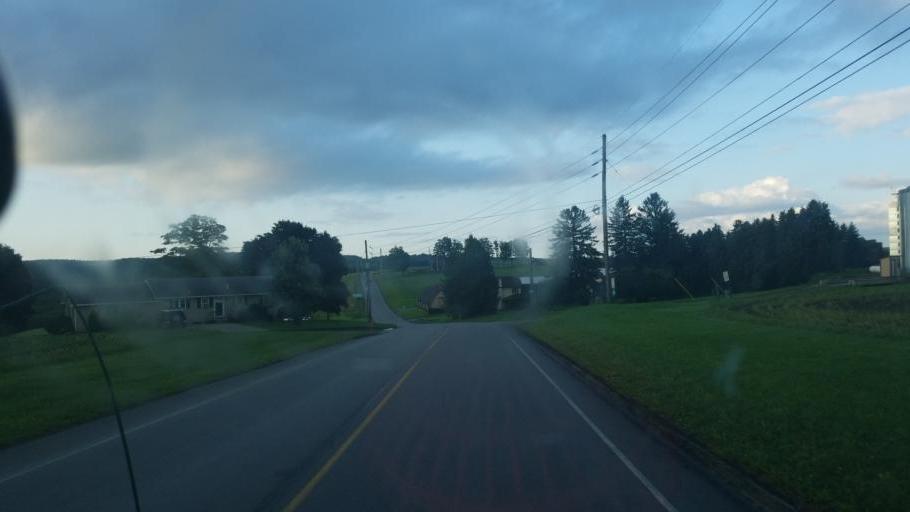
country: US
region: Pennsylvania
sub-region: Potter County
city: Galeton
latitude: 41.8700
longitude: -77.7657
